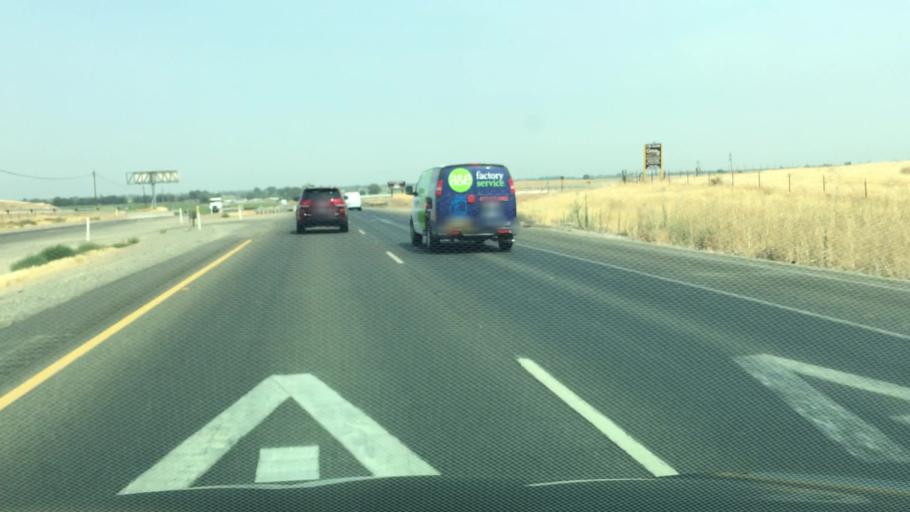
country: US
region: California
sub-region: Merced County
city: Los Banos
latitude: 37.0565
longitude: -120.9488
